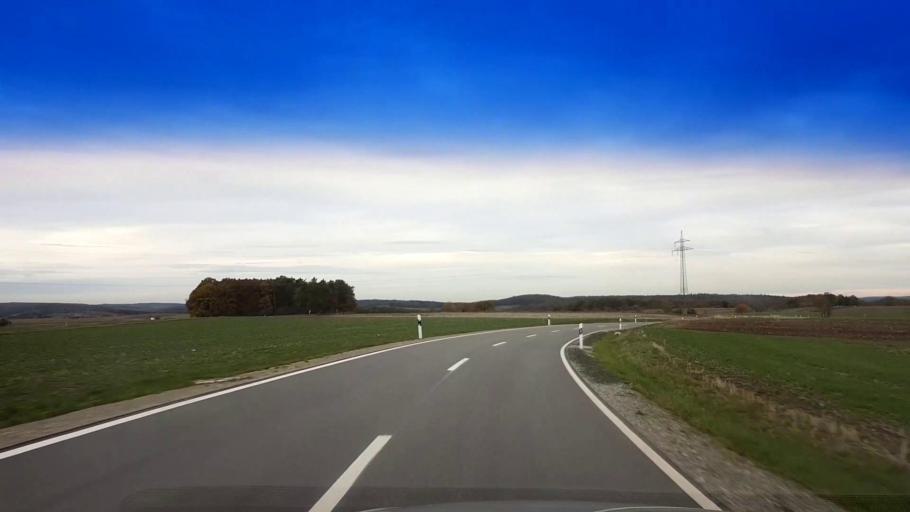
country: DE
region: Bavaria
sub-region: Upper Franconia
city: Priesendorf
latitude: 49.9254
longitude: 10.7074
